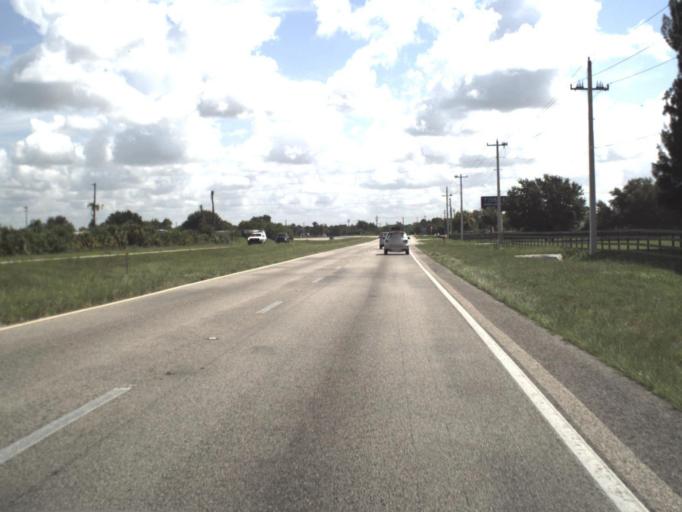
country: US
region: Florida
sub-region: Charlotte County
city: Cleveland
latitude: 26.9449
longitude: -82.0068
